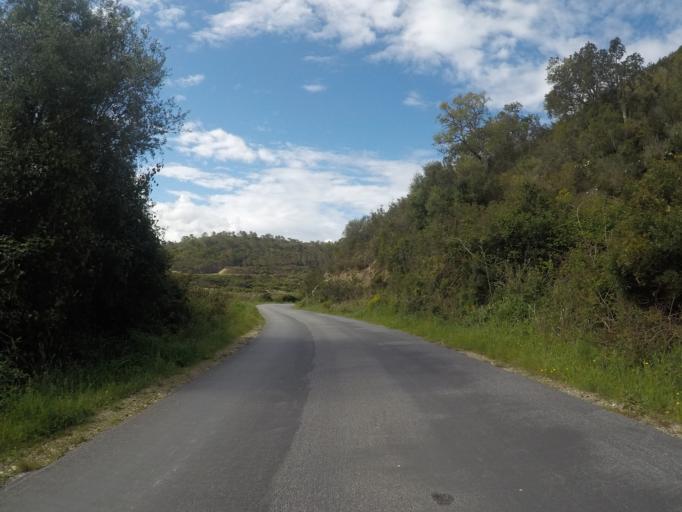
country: PT
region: Beja
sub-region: Odemira
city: Sao Teotonio
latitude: 37.4382
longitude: -8.7903
